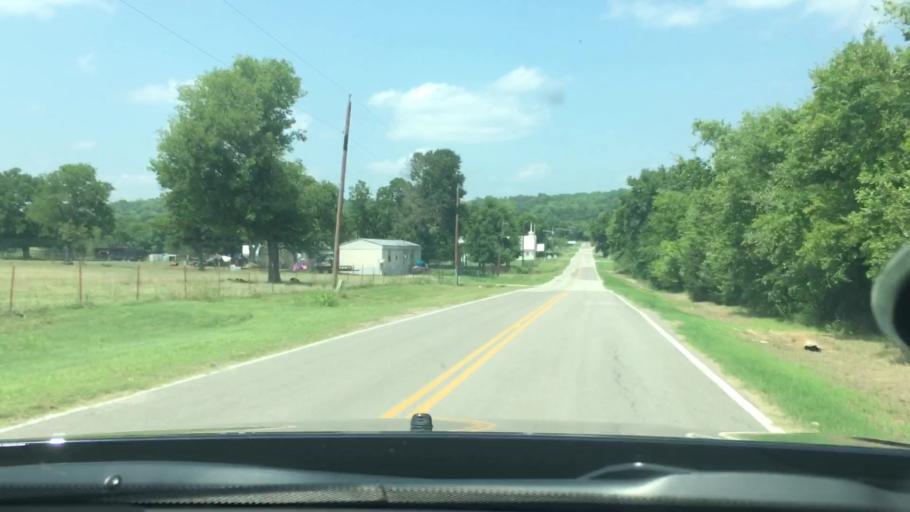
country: US
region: Oklahoma
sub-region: Johnston County
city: Tishomingo
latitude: 34.4140
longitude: -96.4970
